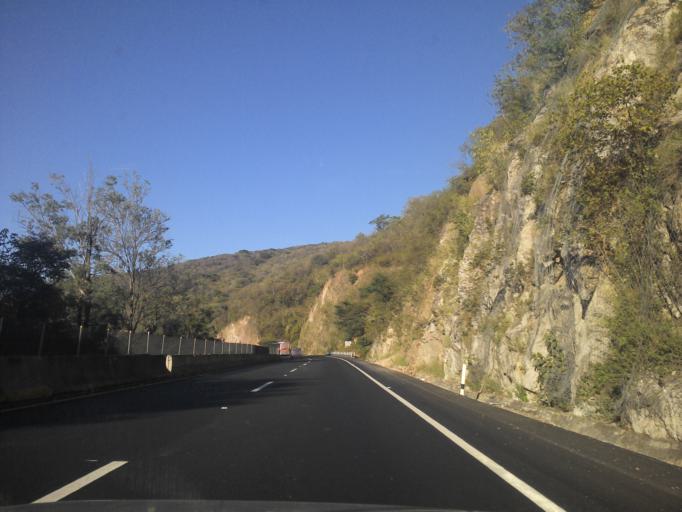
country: MX
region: Jalisco
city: Hostotipaquillo
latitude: 21.0037
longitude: -104.2027
